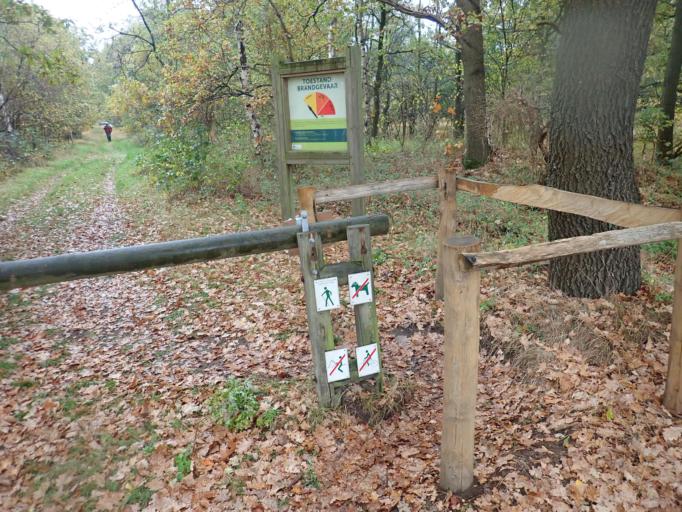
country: BE
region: Flanders
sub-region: Provincie Antwerpen
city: Wuustwezel
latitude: 51.3720
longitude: 4.6123
